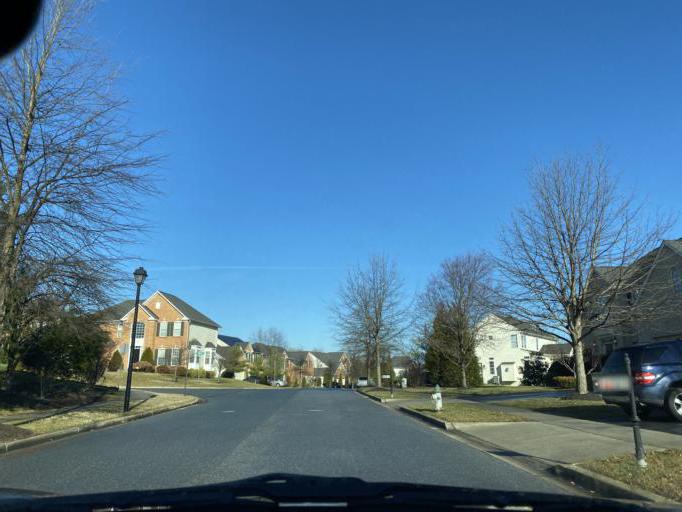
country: US
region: Maryland
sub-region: Prince George's County
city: Laurel
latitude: 39.0870
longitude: -76.8726
